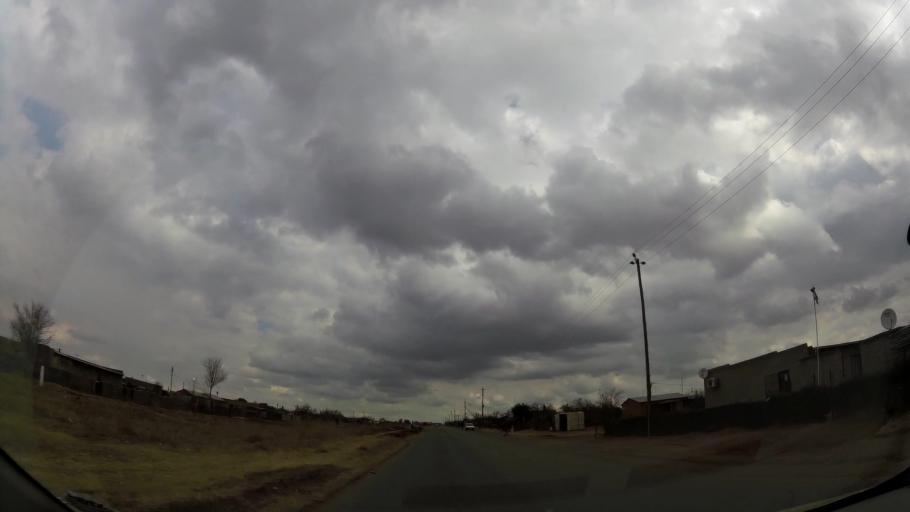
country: ZA
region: Orange Free State
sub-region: Fezile Dabi District Municipality
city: Sasolburg
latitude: -26.8515
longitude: 27.8743
